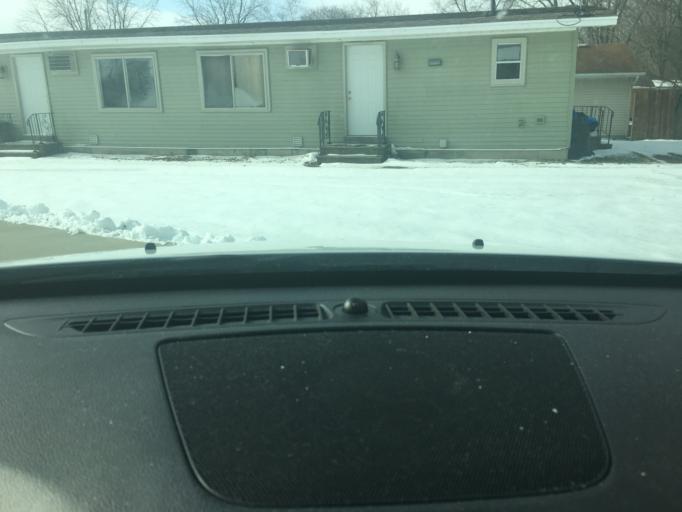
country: US
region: Illinois
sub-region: LaSalle County
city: Ottawa
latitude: 41.3646
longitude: -88.8217
